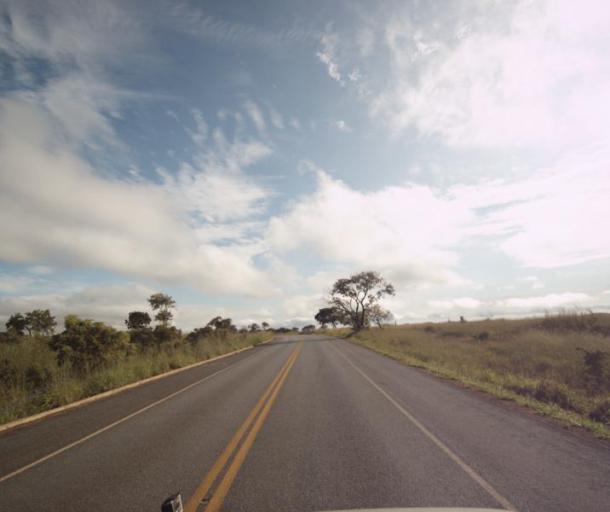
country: BR
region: Goias
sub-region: Padre Bernardo
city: Padre Bernardo
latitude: -15.4643
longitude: -48.6136
